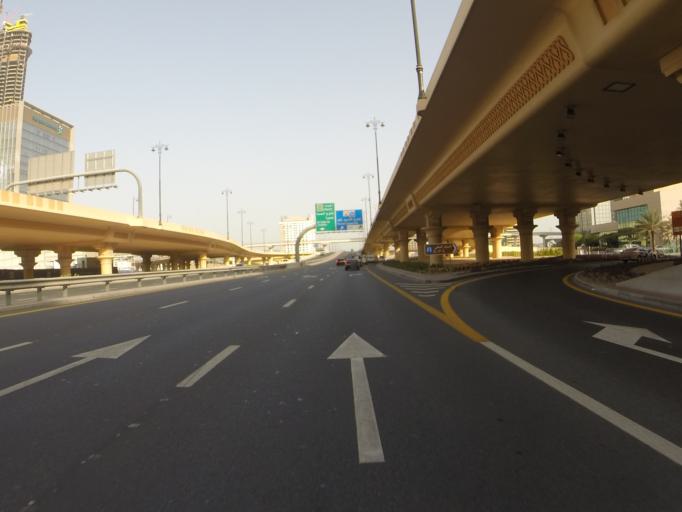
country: AE
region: Dubai
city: Dubai
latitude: 25.2028
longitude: 55.2750
